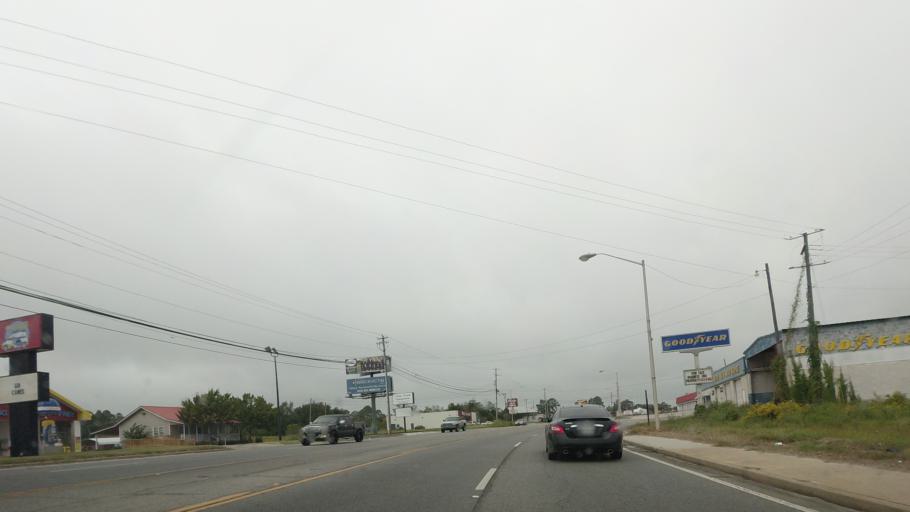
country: US
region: Georgia
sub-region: Ben Hill County
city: Fitzgerald
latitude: 31.7028
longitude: -83.2523
